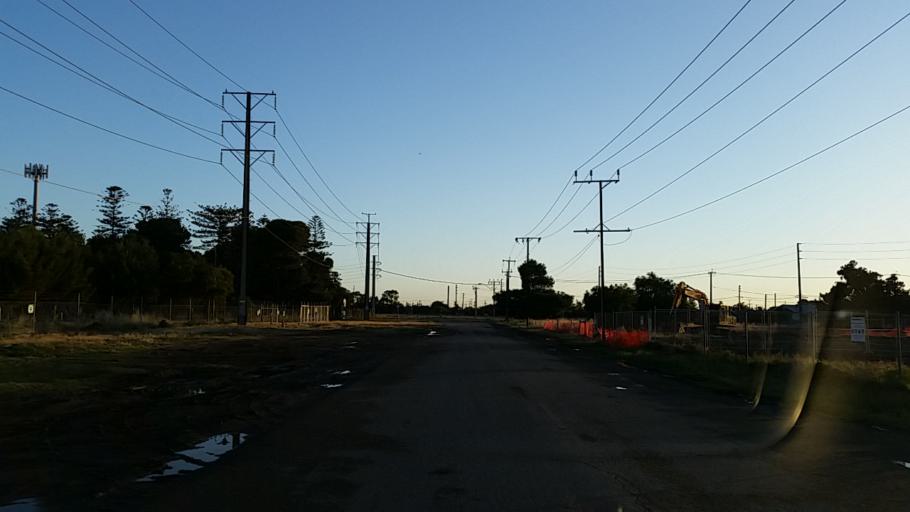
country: AU
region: South Australia
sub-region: Port Adelaide Enfield
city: Birkenhead
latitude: -34.7920
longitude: 138.5053
